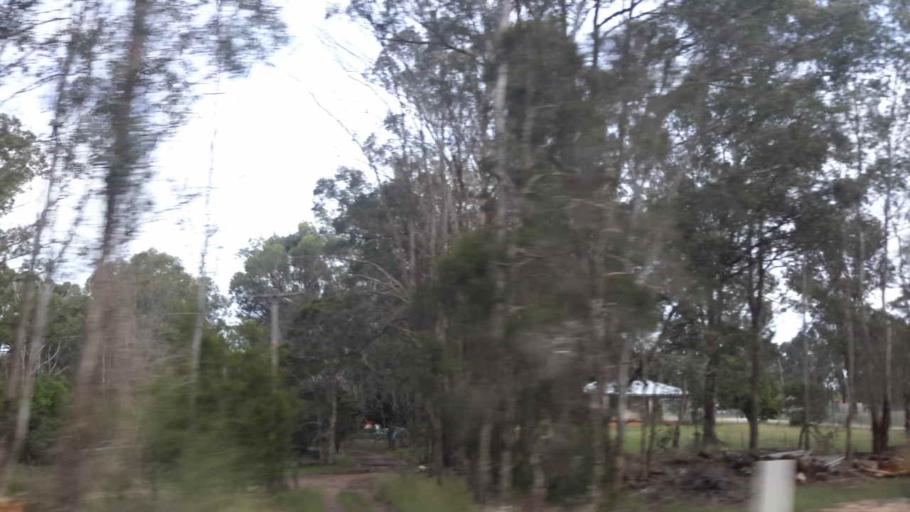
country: AU
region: New South Wales
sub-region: Hawkesbury
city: South Windsor
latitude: -33.6446
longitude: 150.7827
